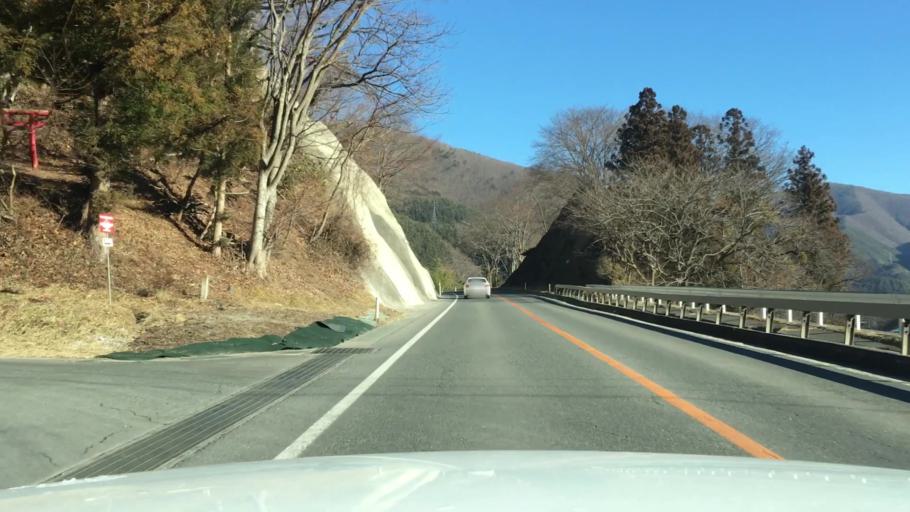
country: JP
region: Iwate
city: Miyako
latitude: 39.5945
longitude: 141.6758
